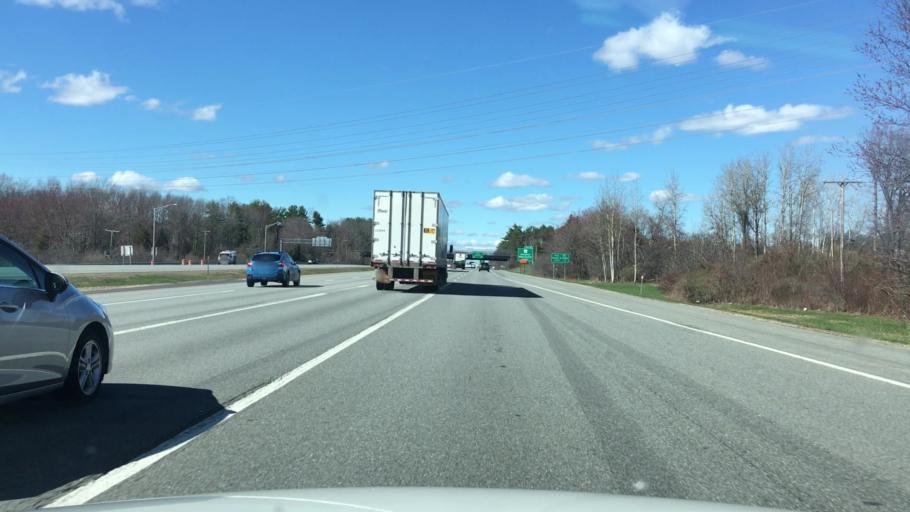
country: US
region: New Hampshire
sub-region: Rockingham County
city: Hampton
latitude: 42.9382
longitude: -70.8610
